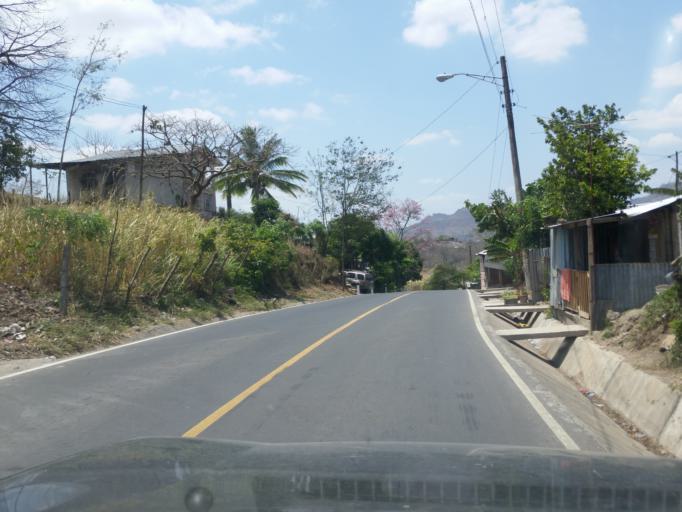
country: NI
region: Boaco
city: Boaco
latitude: 12.4739
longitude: -85.6462
